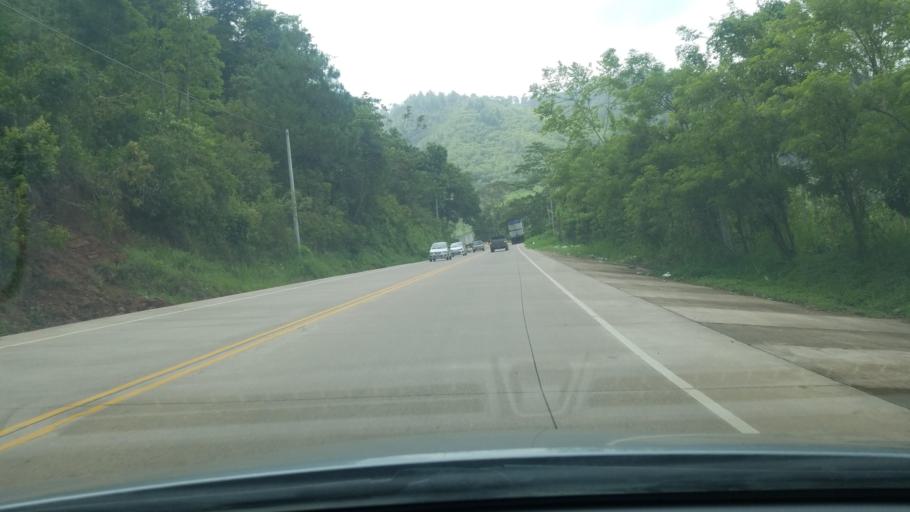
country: HN
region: Copan
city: Buenos Aires
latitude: 14.9207
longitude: -88.9800
